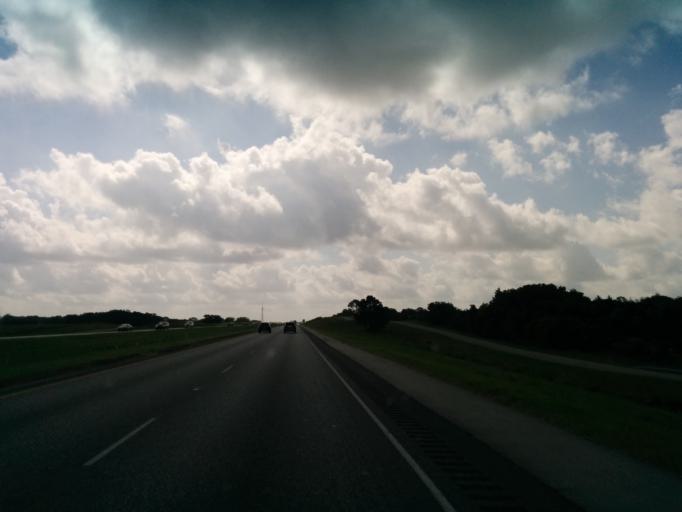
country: US
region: Texas
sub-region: Fayette County
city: Flatonia
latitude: 29.6953
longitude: -97.0304
